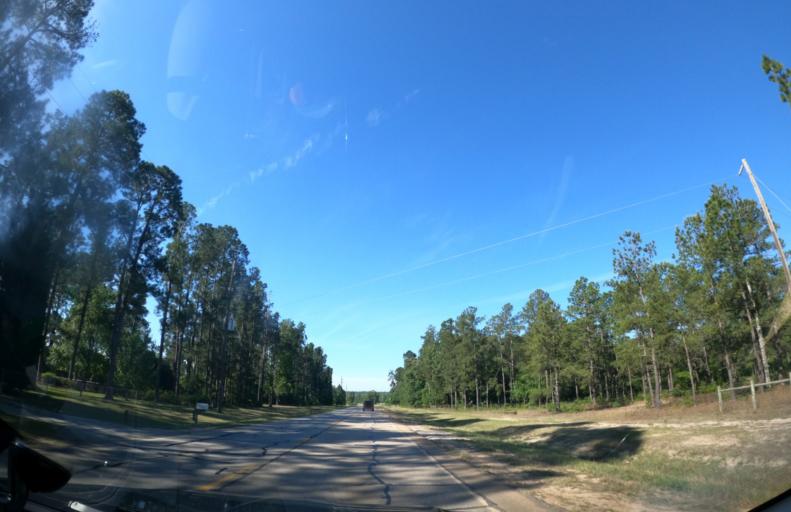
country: US
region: Georgia
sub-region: Jefferson County
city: Wrens
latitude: 33.2840
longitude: -82.3834
